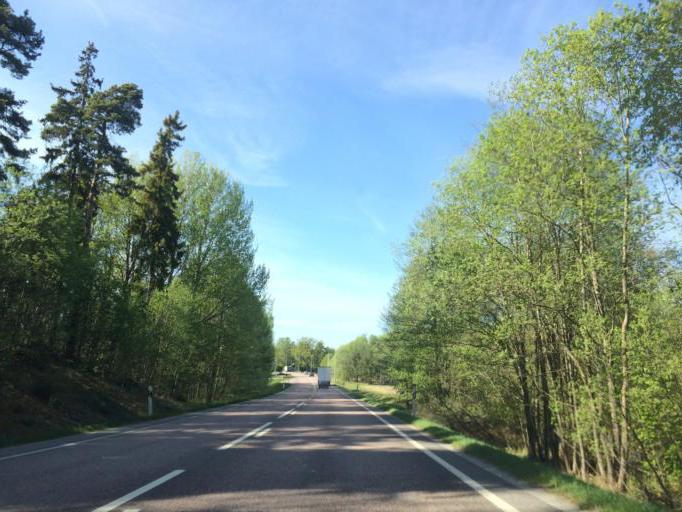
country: SE
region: Vaestmanland
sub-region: Kungsors Kommun
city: Kungsoer
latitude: 59.2812
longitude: 16.1189
